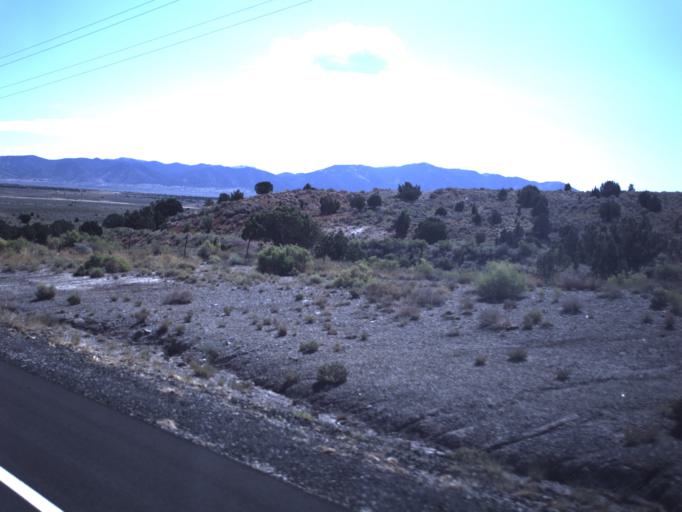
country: US
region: Utah
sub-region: Utah County
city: Eagle Mountain
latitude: 40.0725
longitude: -112.3640
